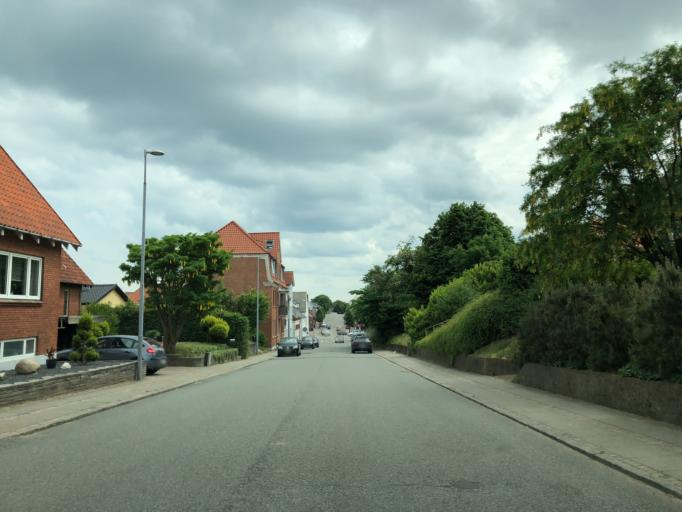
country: DK
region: Central Jutland
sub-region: Struer Kommune
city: Struer
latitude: 56.4911
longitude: 8.5813
